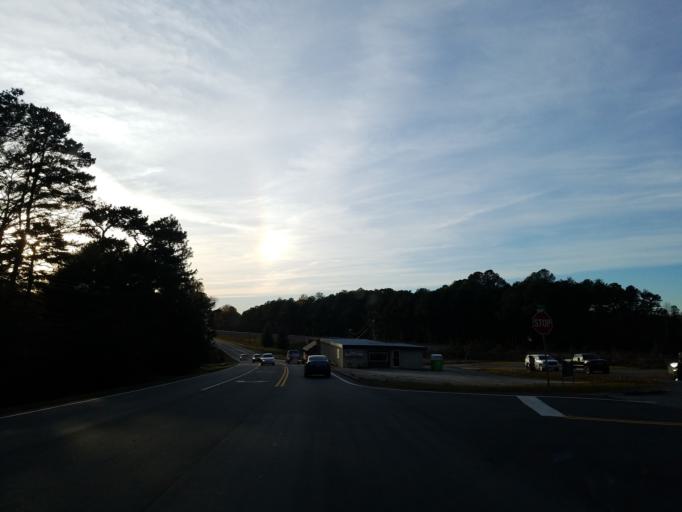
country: US
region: Georgia
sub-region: Haralson County
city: Bremen
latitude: 33.7246
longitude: -85.1353
